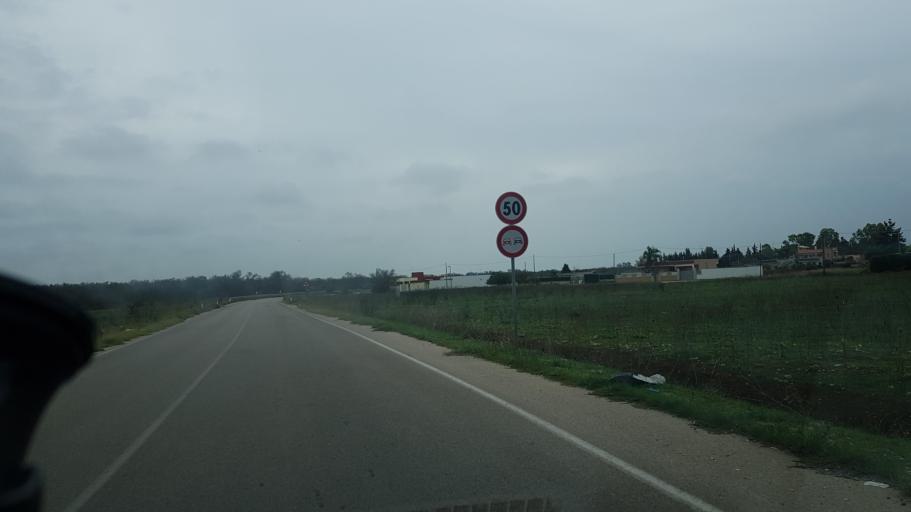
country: IT
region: Apulia
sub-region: Provincia di Brindisi
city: San Pietro Vernotico
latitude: 40.4852
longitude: 18.0114
